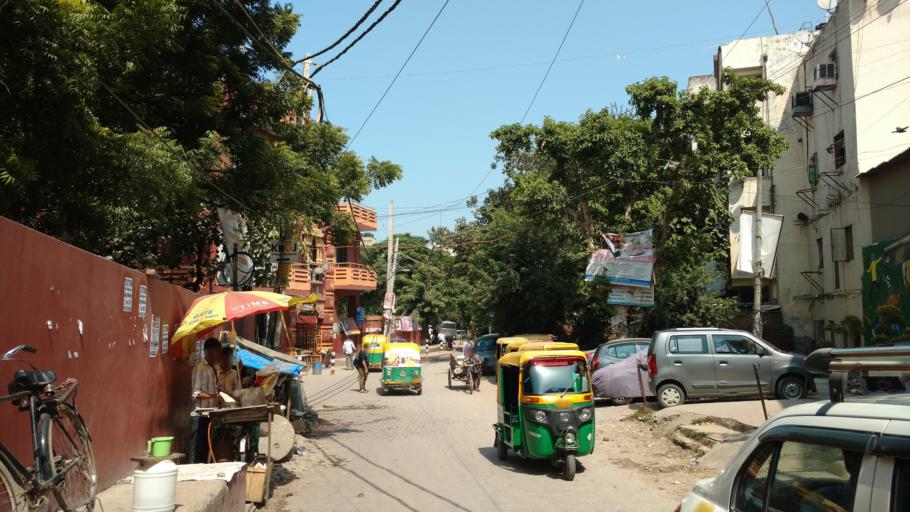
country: IN
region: NCT
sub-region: New Delhi
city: New Delhi
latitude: 28.5309
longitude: 77.2186
